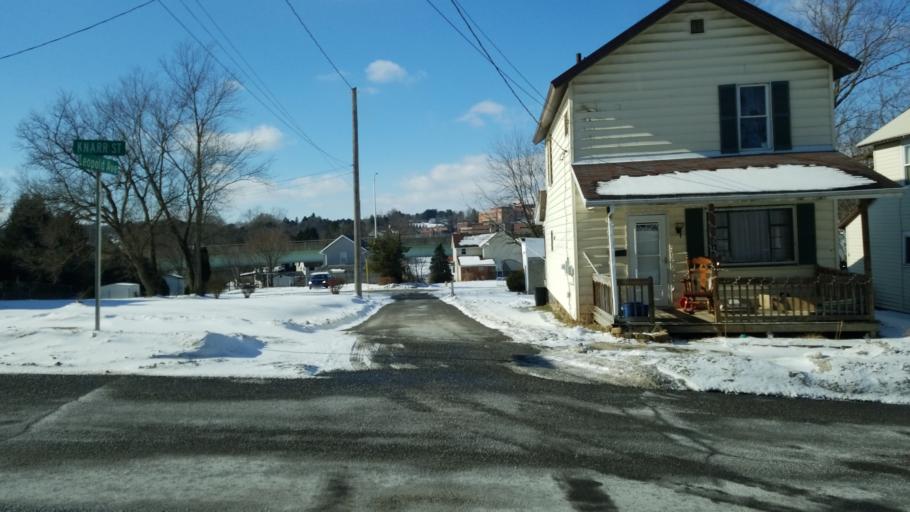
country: US
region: Pennsylvania
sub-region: Clearfield County
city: Sandy
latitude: 41.1119
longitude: -78.7677
